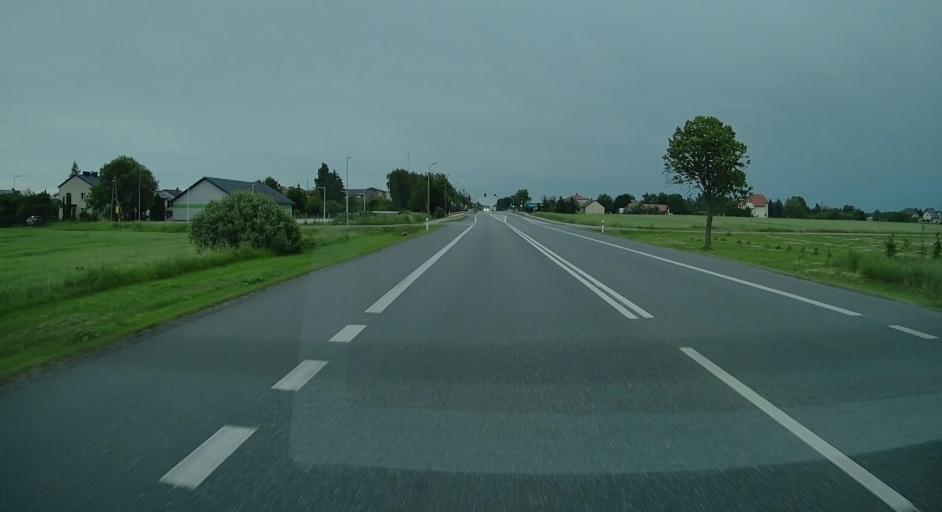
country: PL
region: Lublin Voivodeship
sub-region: Powiat bialski
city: Zalesie
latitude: 52.0355
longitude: 23.3587
